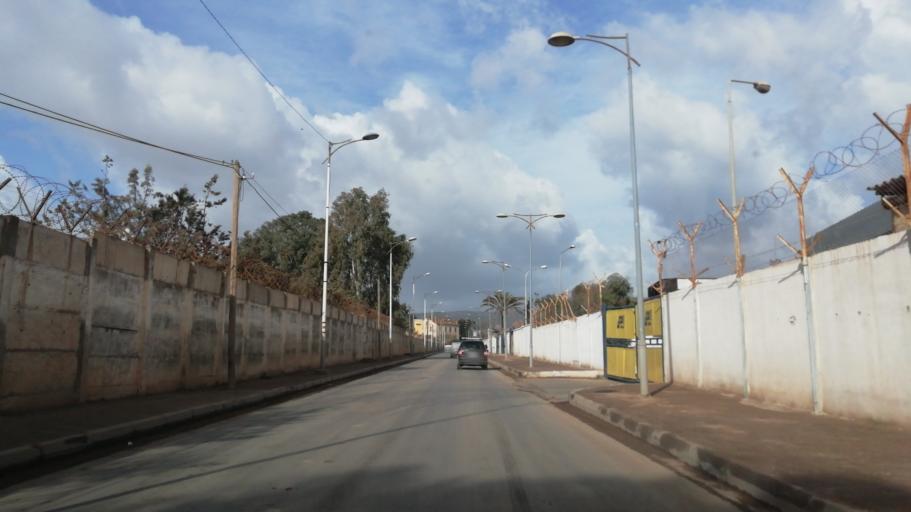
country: DZ
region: Oran
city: Oran
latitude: 35.6782
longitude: -0.6218
